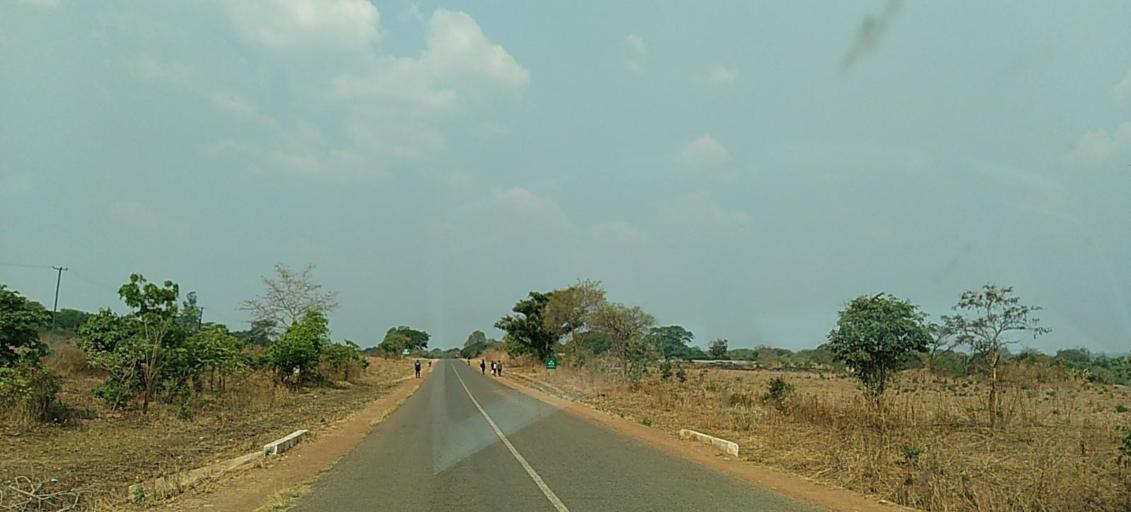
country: ZM
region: North-Western
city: Kabompo
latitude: -13.5907
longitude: 24.2168
